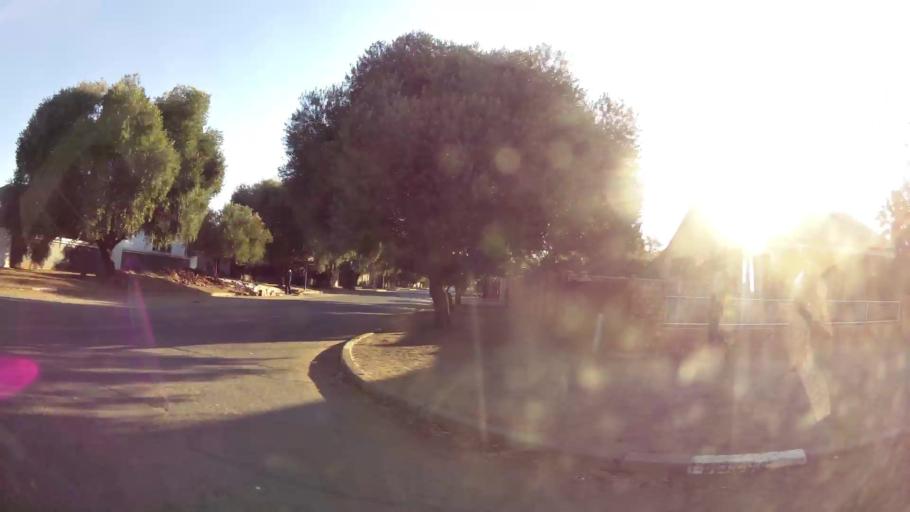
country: ZA
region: Northern Cape
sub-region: Frances Baard District Municipality
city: Kimberley
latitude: -28.7378
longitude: 24.7422
